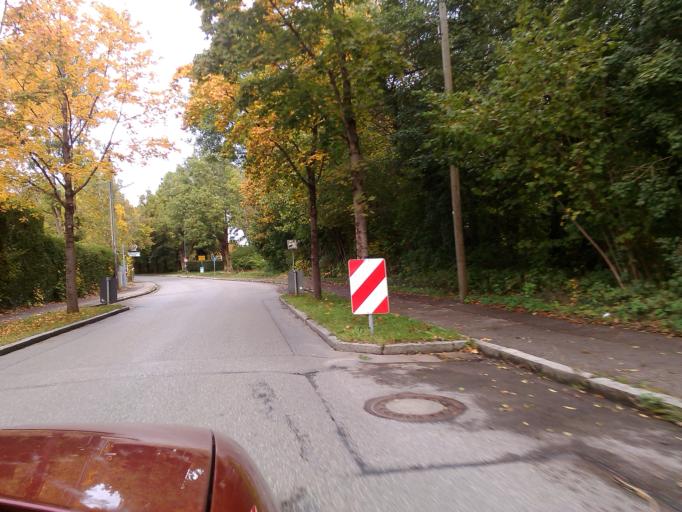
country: DE
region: Bavaria
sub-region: Upper Bavaria
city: Grafelfing
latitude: 48.1113
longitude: 11.4285
